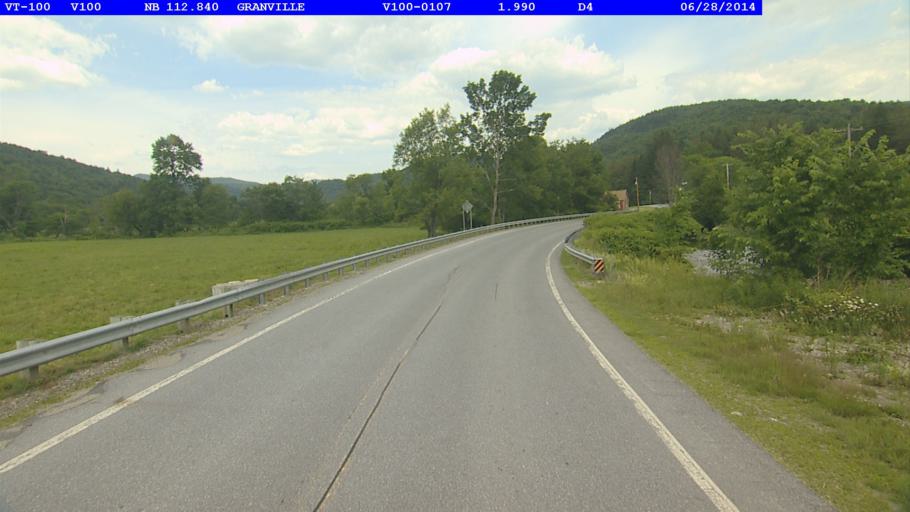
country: US
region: Vermont
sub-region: Orange County
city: Randolph
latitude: 43.9729
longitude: -72.8432
